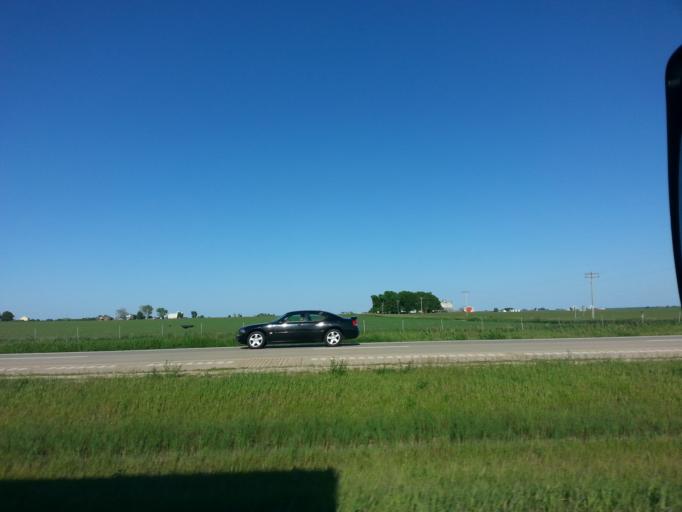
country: US
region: Illinois
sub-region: Woodford County
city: El Paso
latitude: 40.7227
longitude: -89.0343
